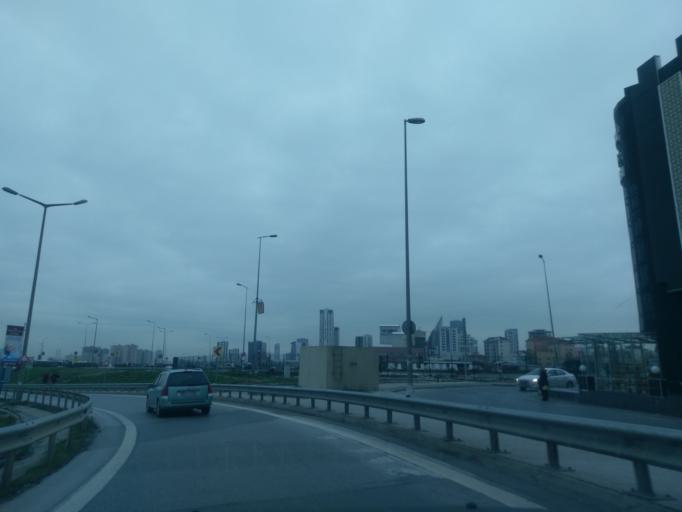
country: TR
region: Istanbul
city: Maltepe
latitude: 40.9075
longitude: 29.2110
